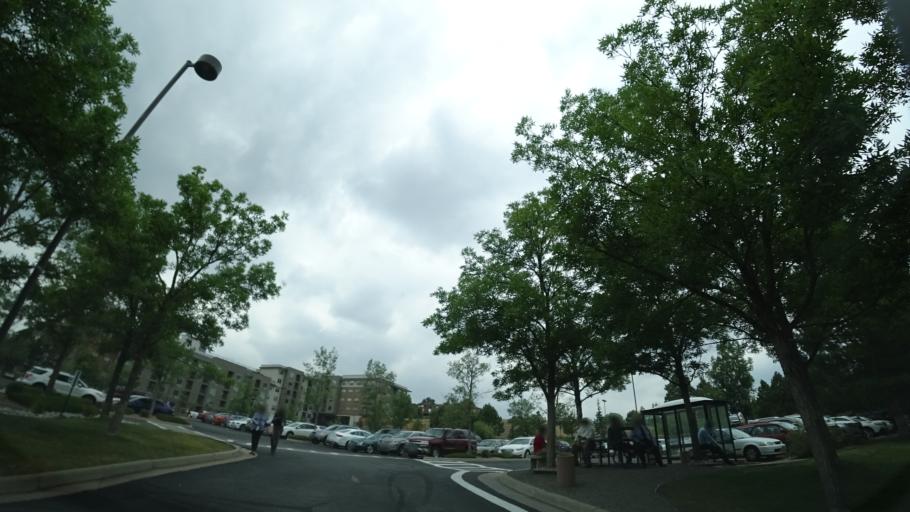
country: US
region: Colorado
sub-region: Jefferson County
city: West Pleasant View
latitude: 39.7165
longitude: -105.1380
